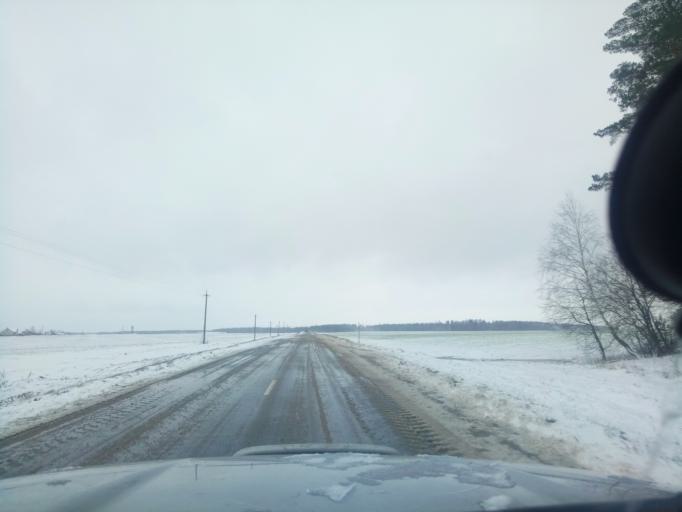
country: BY
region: Minsk
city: Tsimkavichy
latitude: 53.0435
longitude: 26.8483
